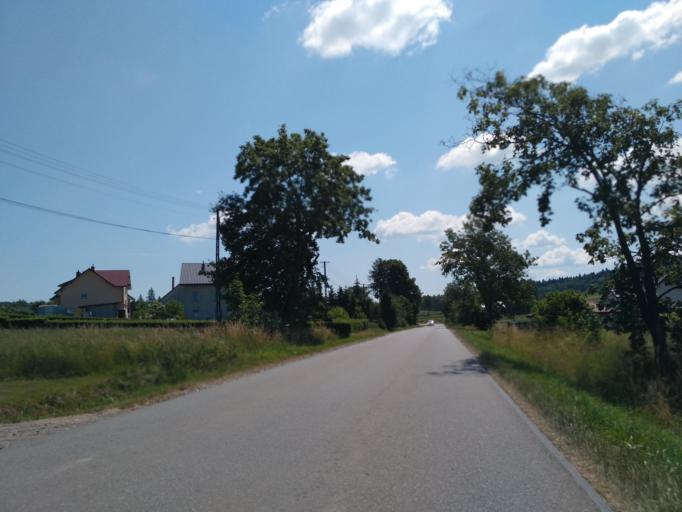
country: PL
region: Subcarpathian Voivodeship
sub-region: Powiat sanocki
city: Niebieszczany
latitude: 49.4957
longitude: 22.1674
